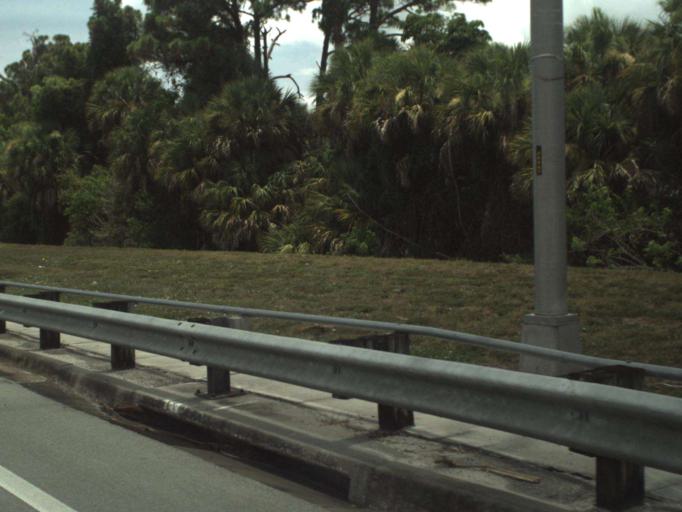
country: US
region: Florida
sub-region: Saint Lucie County
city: Fort Pierce South
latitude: 27.4255
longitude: -80.3408
